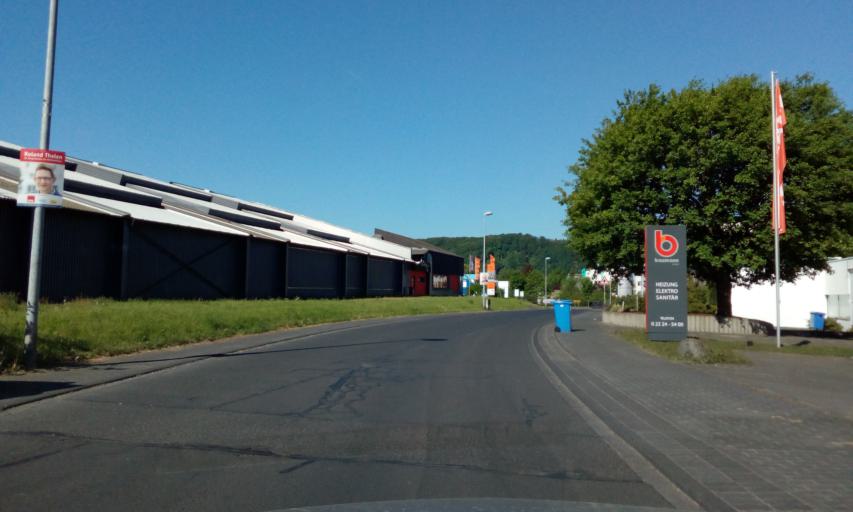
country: DE
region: Rheinland-Pfalz
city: Rheinbreitbach
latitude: 50.6243
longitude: 7.2276
